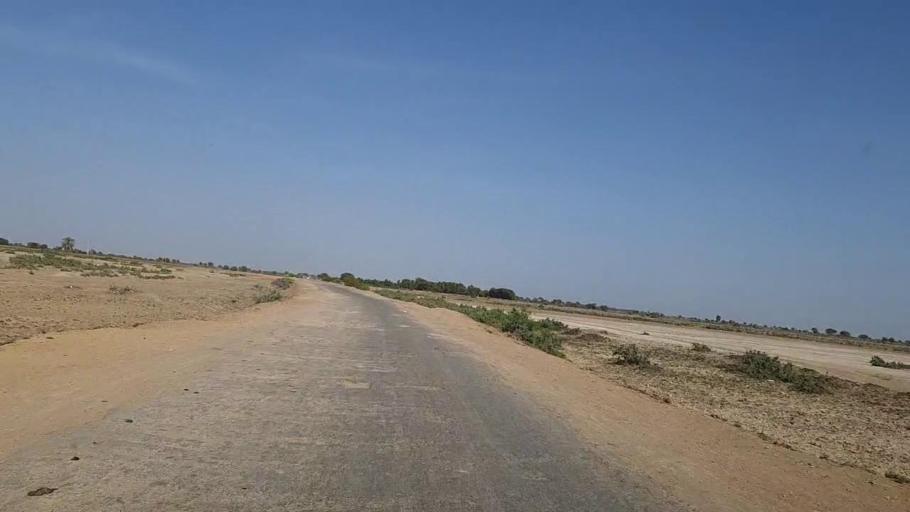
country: PK
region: Sindh
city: Kotri
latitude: 25.1595
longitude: 68.2437
